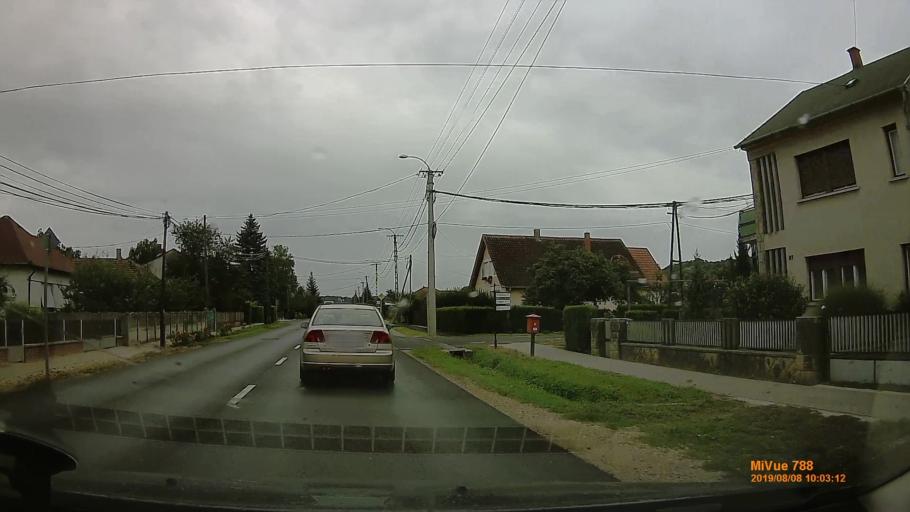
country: HU
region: Zala
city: Zalaegerszeg
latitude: 46.9314
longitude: 16.8559
